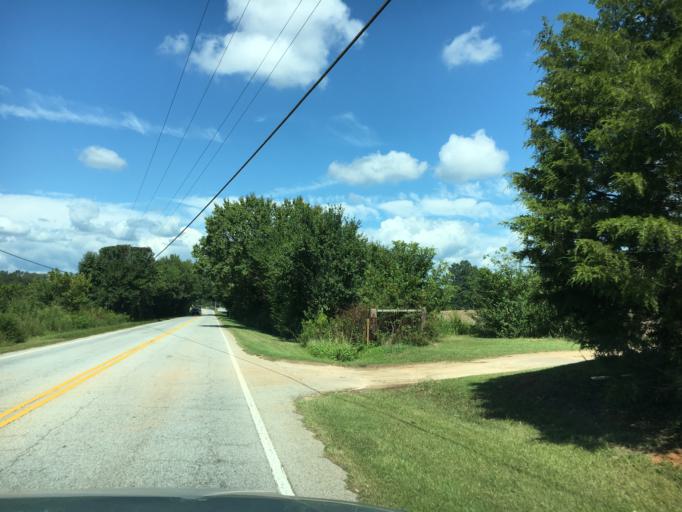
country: US
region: South Carolina
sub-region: Greenville County
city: Tigerville
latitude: 35.0028
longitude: -82.3585
